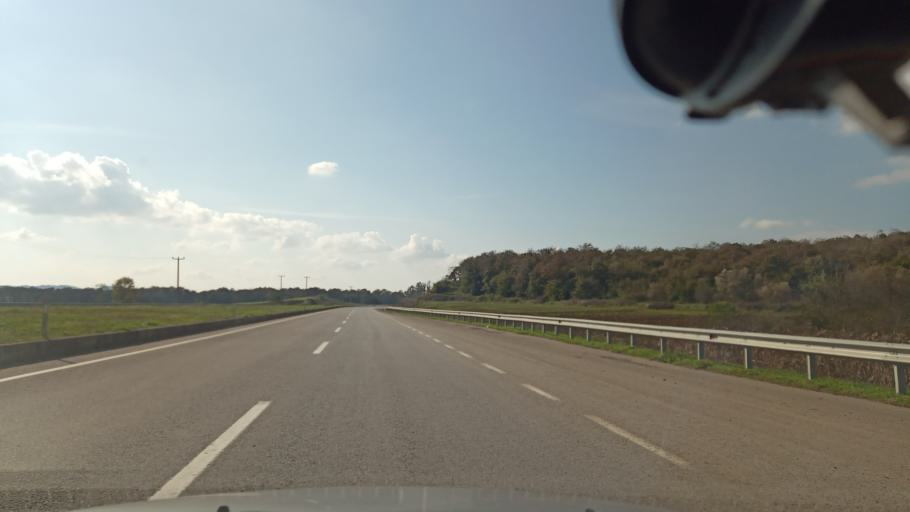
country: TR
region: Sakarya
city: Kaynarca
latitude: 41.0622
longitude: 30.3540
